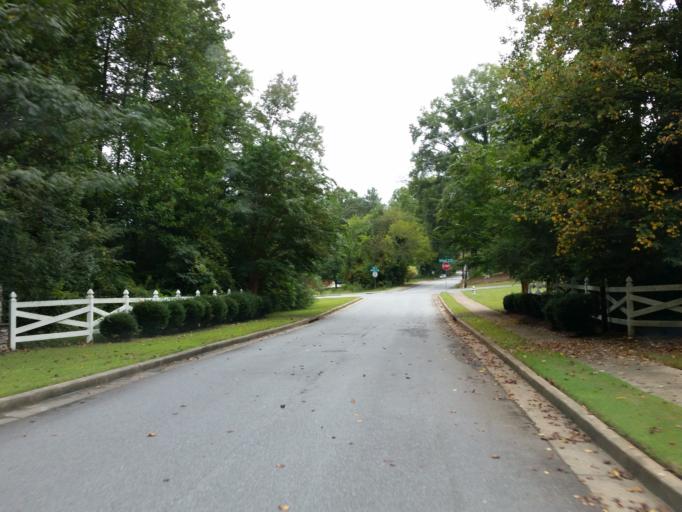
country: US
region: Georgia
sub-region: Cobb County
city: Marietta
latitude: 33.9669
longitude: -84.5393
